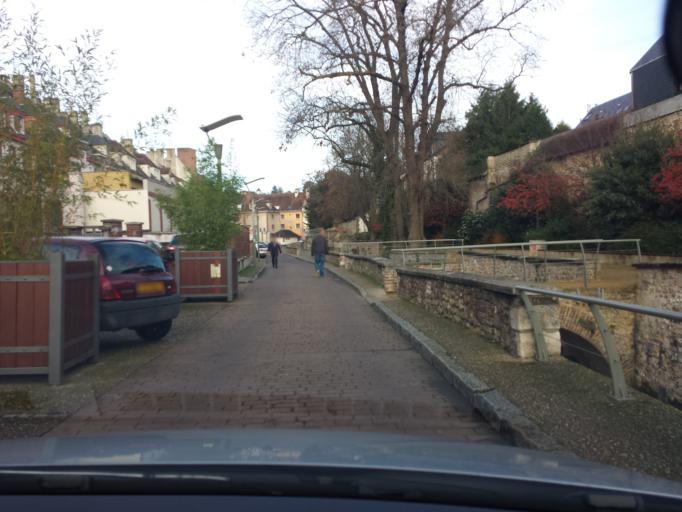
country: FR
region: Haute-Normandie
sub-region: Departement de l'Eure
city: Evreux
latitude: 49.0245
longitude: 1.1494
